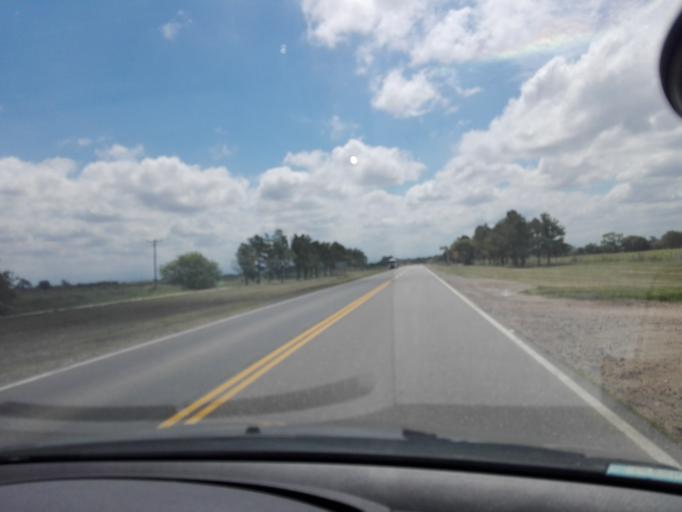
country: AR
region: Cordoba
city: Toledo
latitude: -31.6500
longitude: -64.0936
